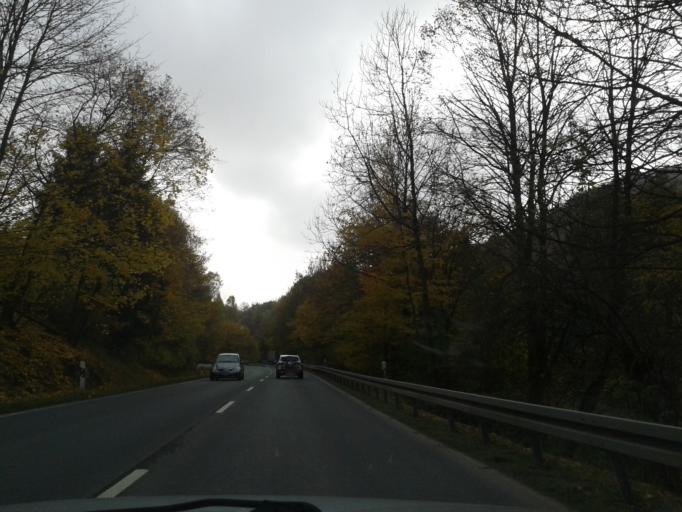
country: DE
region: North Rhine-Westphalia
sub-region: Regierungsbezirk Arnsberg
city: Winterberg
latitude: 51.2712
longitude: 8.5199
